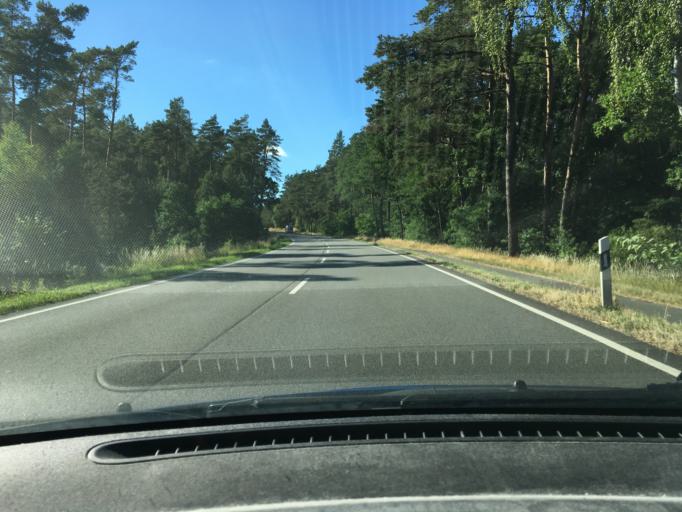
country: DE
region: Lower Saxony
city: Reinstorf
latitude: 53.2088
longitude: 10.6033
